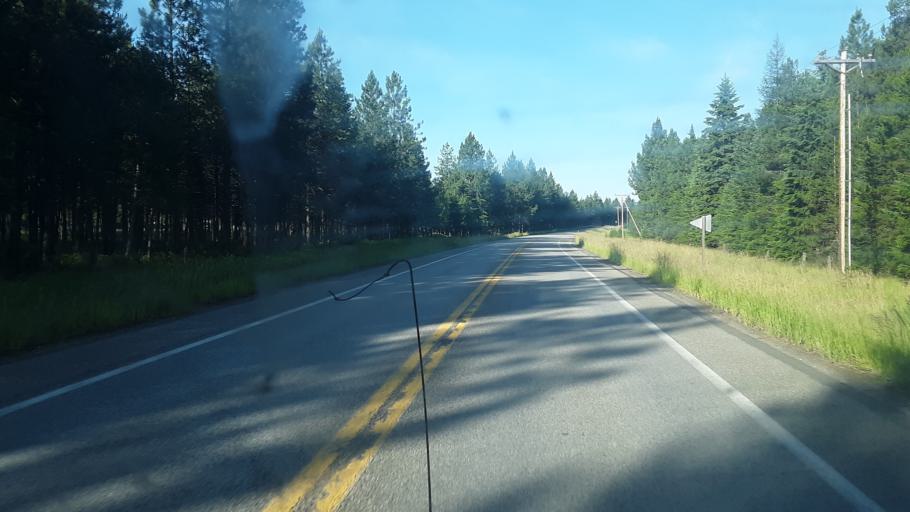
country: US
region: Idaho
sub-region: Boundary County
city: Bonners Ferry
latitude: 48.7309
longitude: -116.1929
